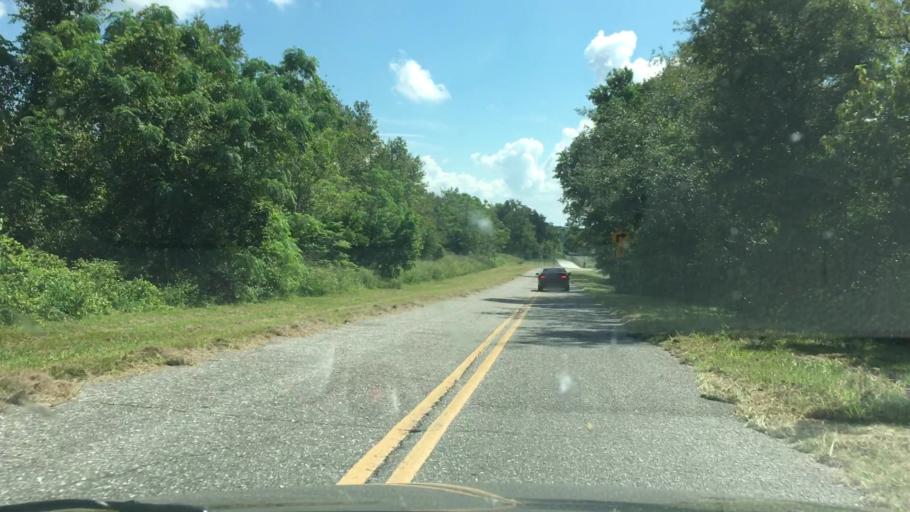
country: US
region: Florida
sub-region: Lake County
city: Montverde
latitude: 28.6374
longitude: -81.7162
